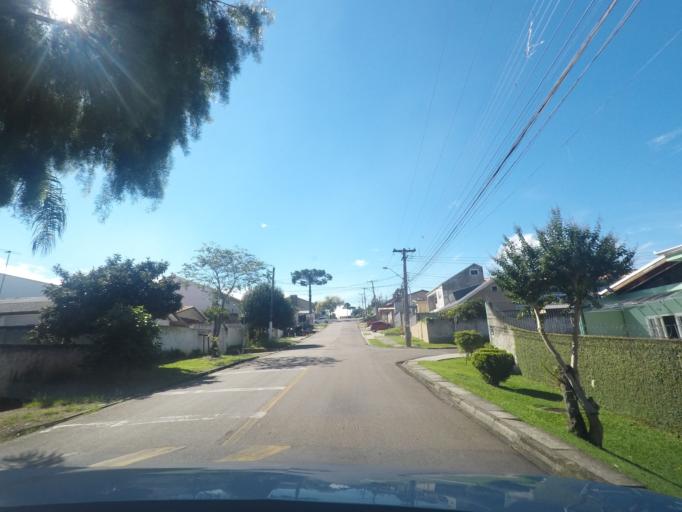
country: BR
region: Parana
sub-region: Sao Jose Dos Pinhais
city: Sao Jose dos Pinhais
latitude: -25.5037
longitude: -49.2679
